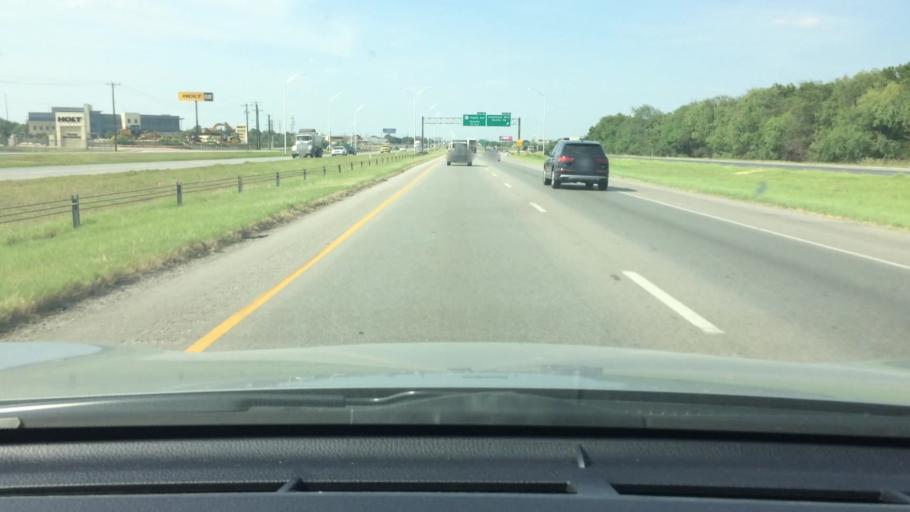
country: US
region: Texas
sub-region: Bexar County
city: China Grove
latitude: 29.3674
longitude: -98.3963
